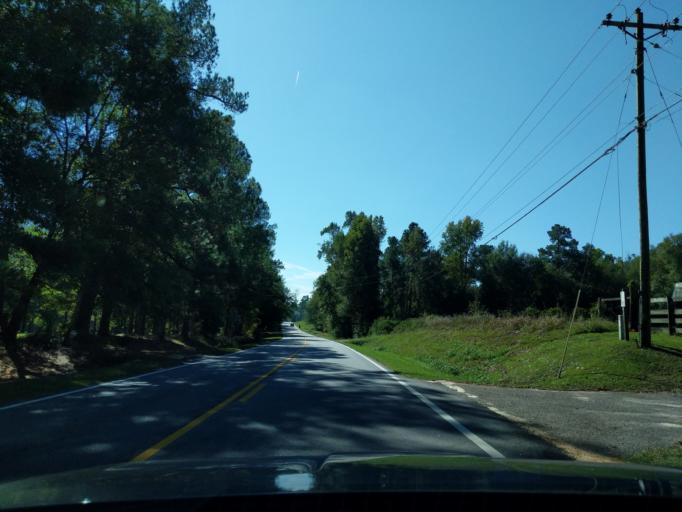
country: US
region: Georgia
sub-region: Richmond County
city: Hephzibah
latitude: 33.3149
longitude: -82.0190
